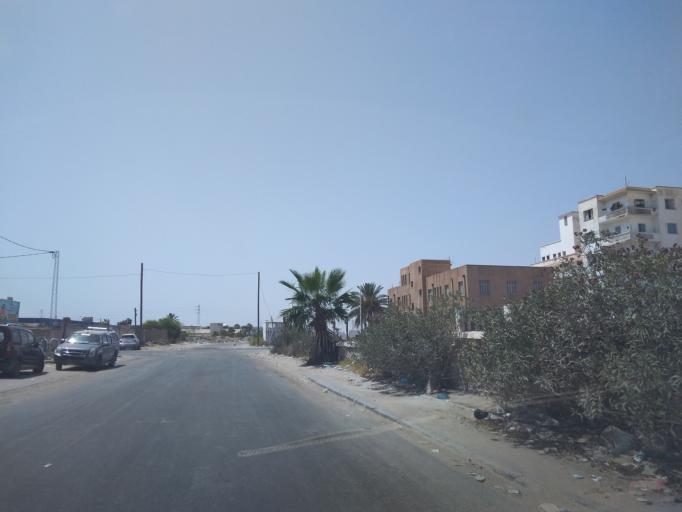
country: TN
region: Safaqis
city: Sfax
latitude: 34.7275
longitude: 10.7634
